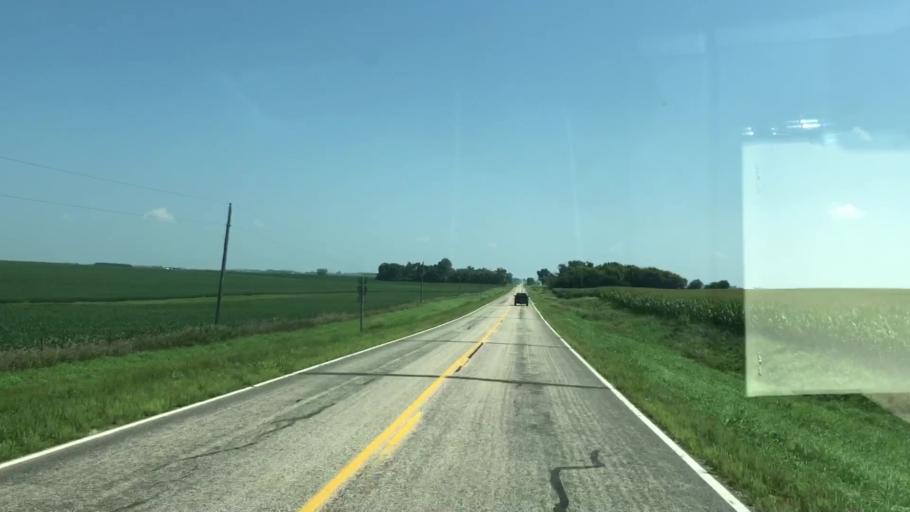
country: US
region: Iowa
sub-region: O'Brien County
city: Sanborn
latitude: 43.2728
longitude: -95.7223
